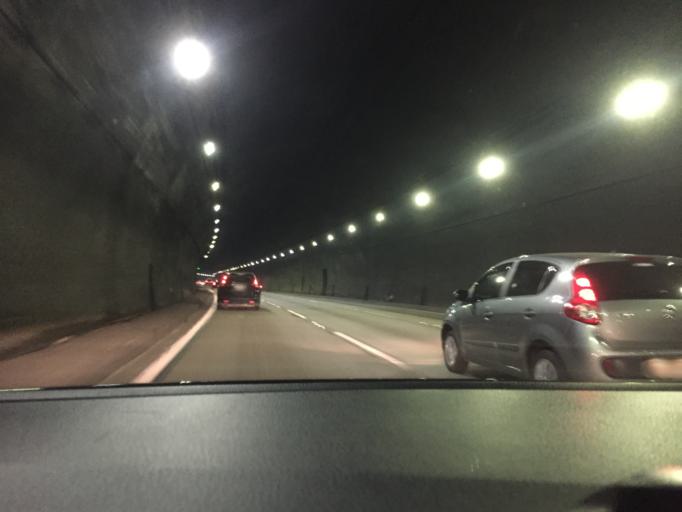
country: BR
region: Sao Paulo
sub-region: Cubatao
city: Cubatao
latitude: -23.8909
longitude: -46.5037
